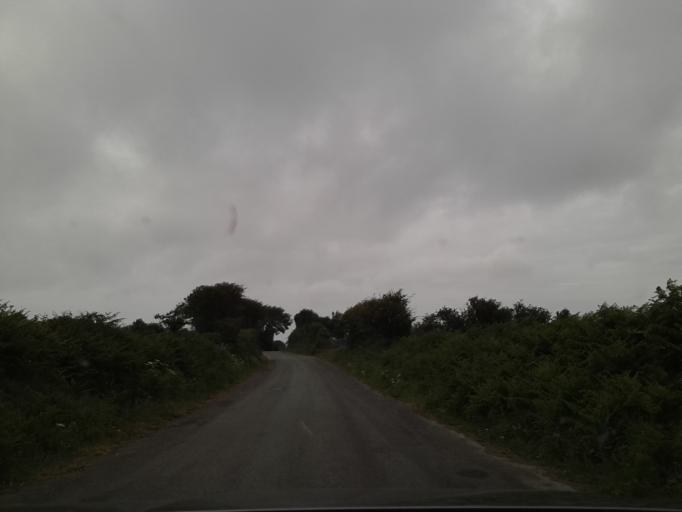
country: FR
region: Lower Normandy
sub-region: Departement de la Manche
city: Beaumont-Hague
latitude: 49.6860
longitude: -1.8703
